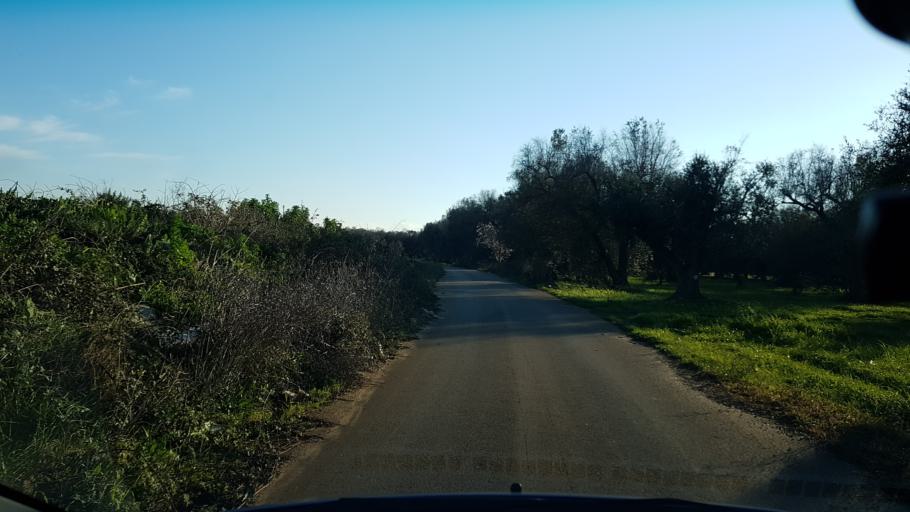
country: IT
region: Apulia
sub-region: Provincia di Brindisi
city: Mesagne
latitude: 40.5643
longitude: 17.8683
